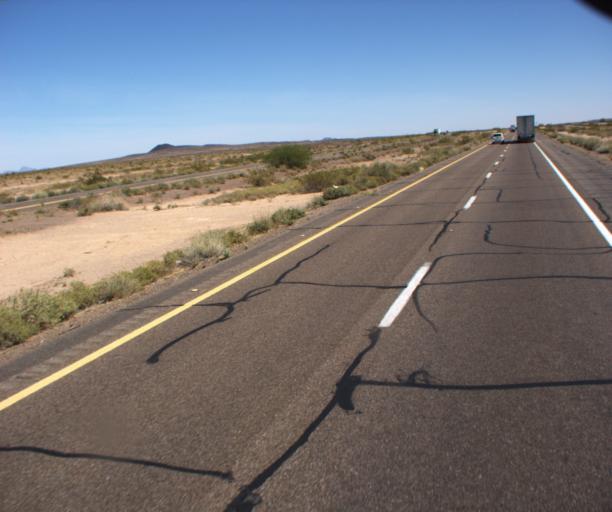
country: US
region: Arizona
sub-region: Maricopa County
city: Gila Bend
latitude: 32.8620
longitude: -113.1746
